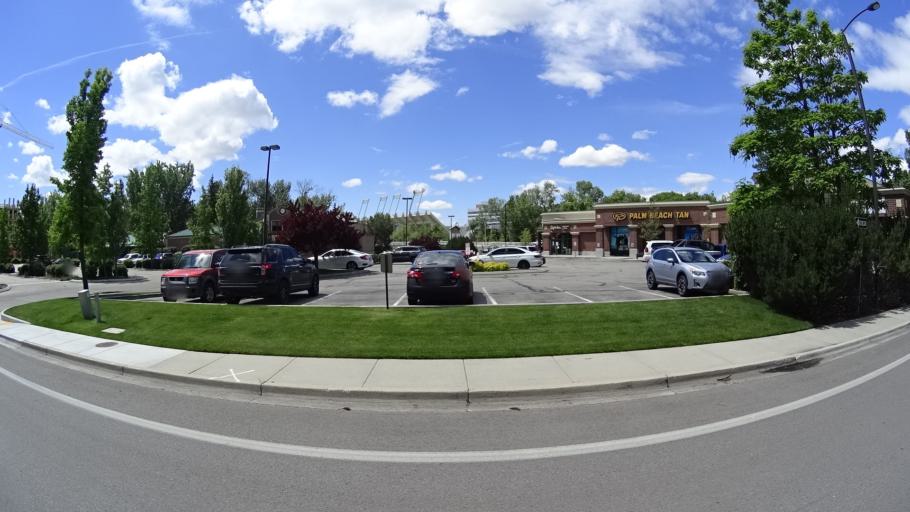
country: US
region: Idaho
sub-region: Ada County
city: Boise
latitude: 43.6053
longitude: -116.1923
